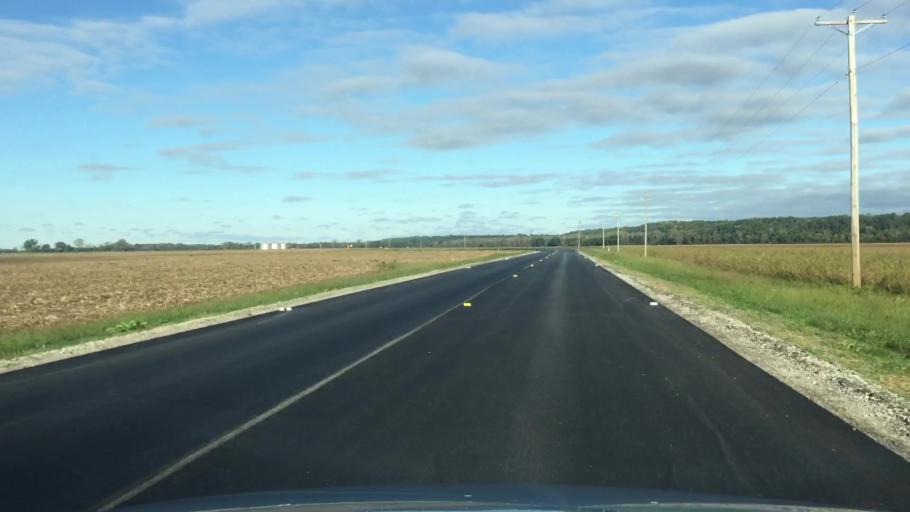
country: US
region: Missouri
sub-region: Howard County
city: New Franklin
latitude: 38.9983
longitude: -92.6717
